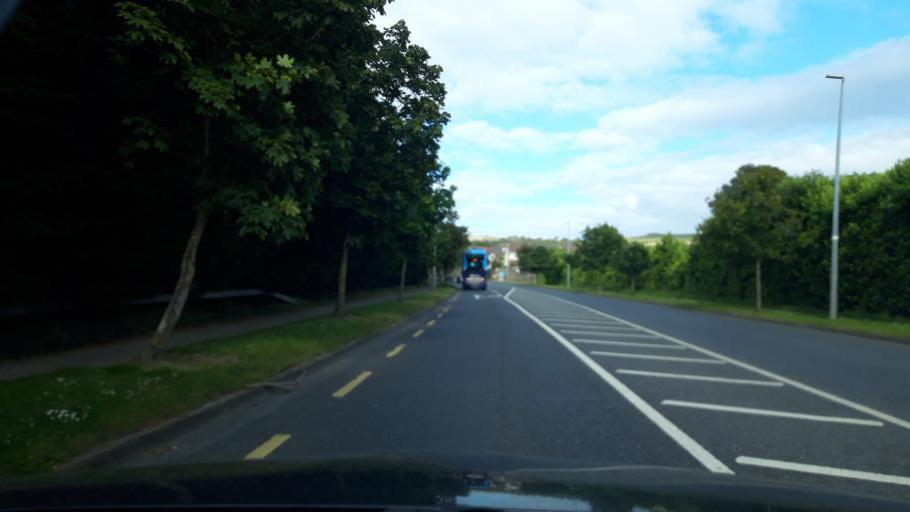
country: IE
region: Leinster
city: Little Bray
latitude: 53.1842
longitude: -6.1115
